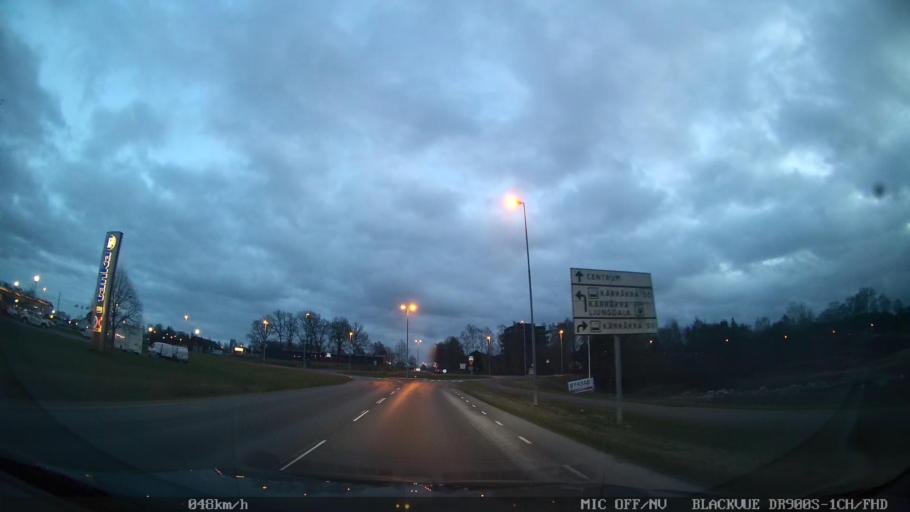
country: SE
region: Skane
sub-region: Hassleholms Kommun
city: Hassleholm
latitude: 56.1697
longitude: 13.7572
